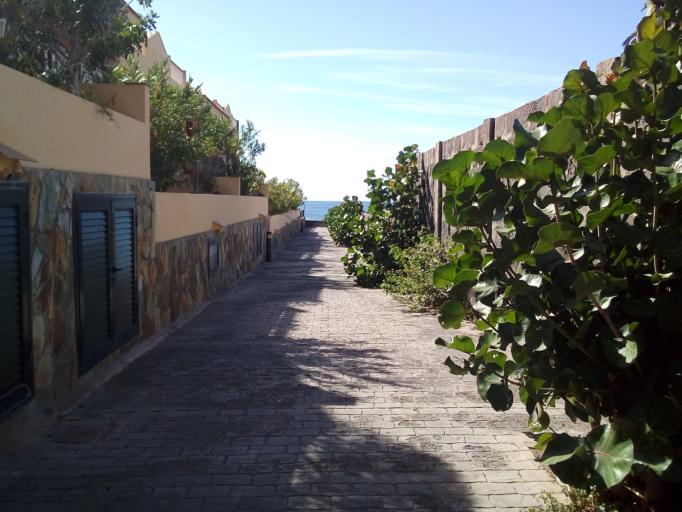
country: ES
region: Canary Islands
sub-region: Provincia de Santa Cruz de Tenerife
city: Alajero
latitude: 28.0962
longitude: -17.3443
